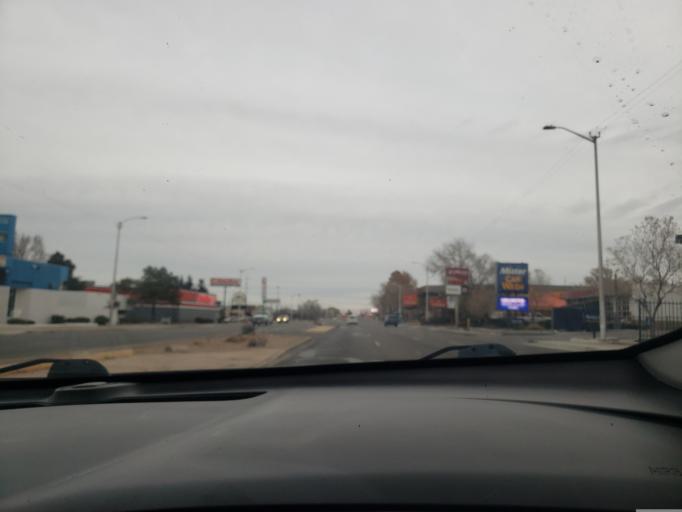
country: US
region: New Mexico
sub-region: Bernalillo County
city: North Valley
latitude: 35.1277
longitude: -106.5864
